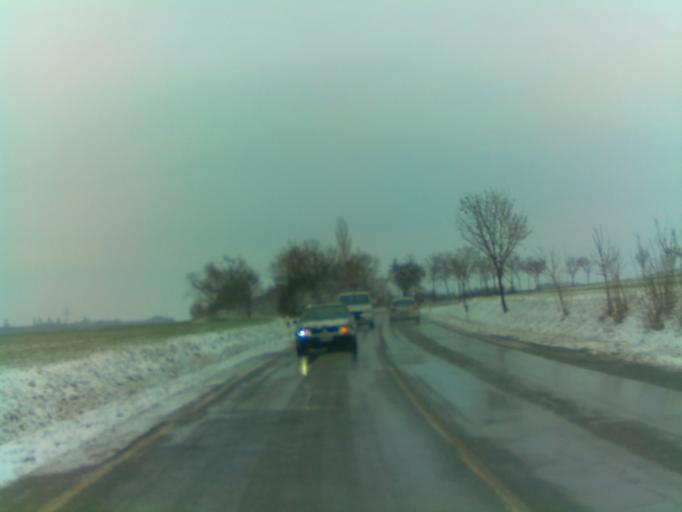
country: DE
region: Thuringia
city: Alkersleben
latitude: 50.8191
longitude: 11.0215
